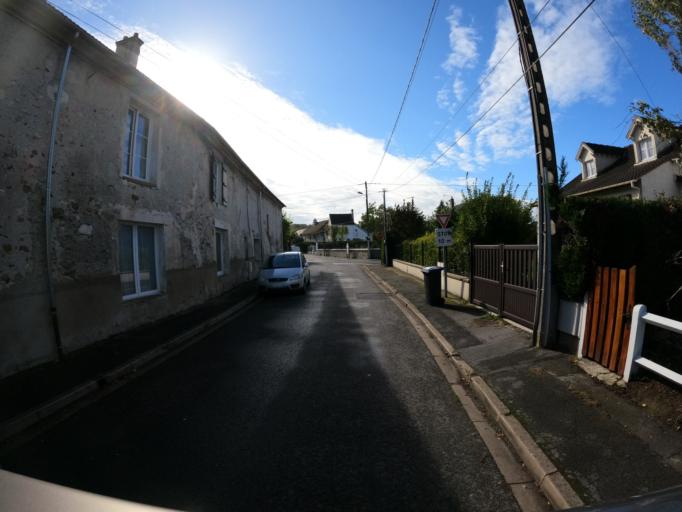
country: FR
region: Ile-de-France
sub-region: Departement de Seine-et-Marne
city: Saint-Germain-sur-Morin
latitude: 48.8799
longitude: 2.8543
